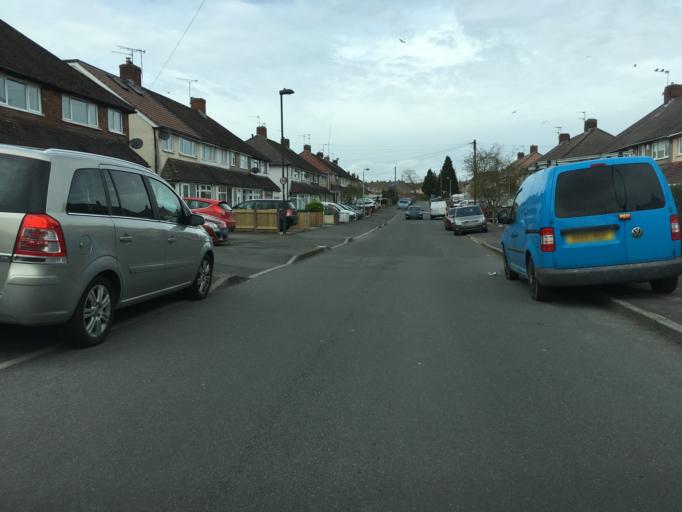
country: GB
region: England
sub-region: South Gloucestershire
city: Almondsbury
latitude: 51.5330
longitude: -2.5841
